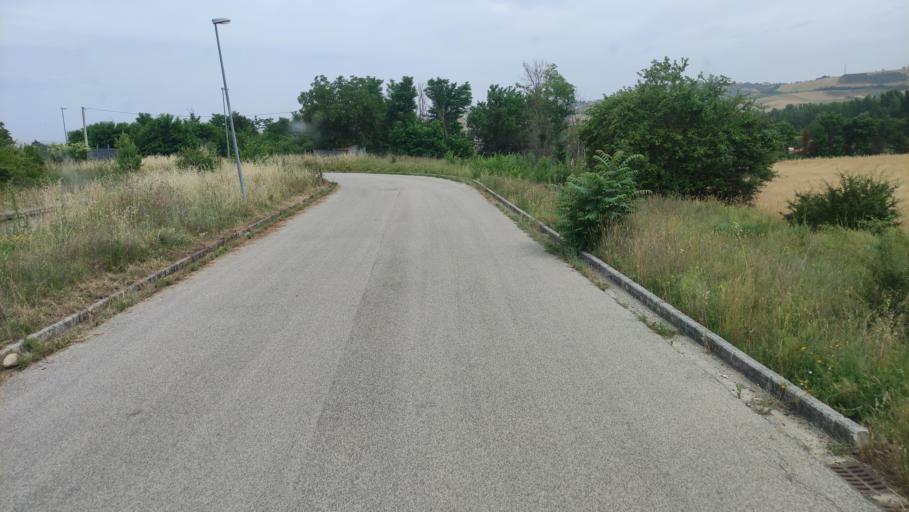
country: IT
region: Campania
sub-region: Provincia di Avellino
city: Sturno
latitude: 41.0483
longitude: 15.1296
